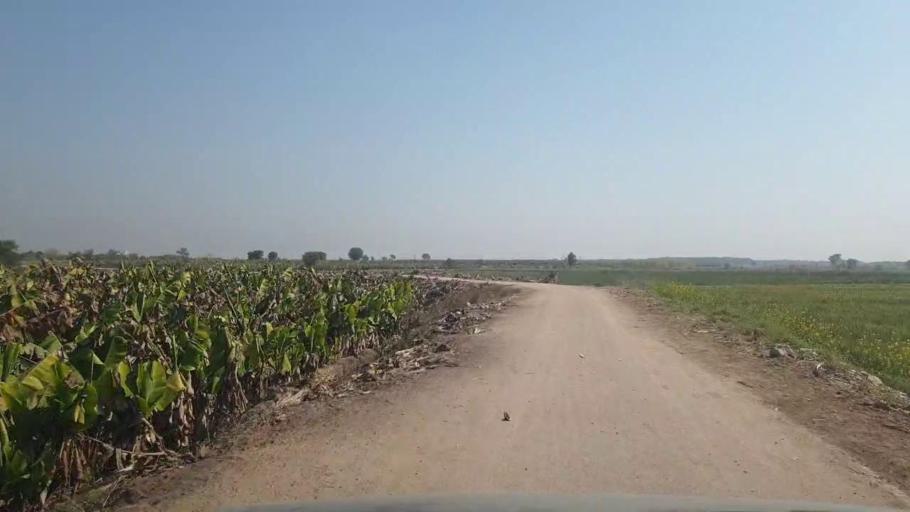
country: PK
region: Sindh
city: Chambar
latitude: 25.3736
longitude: 68.7851
